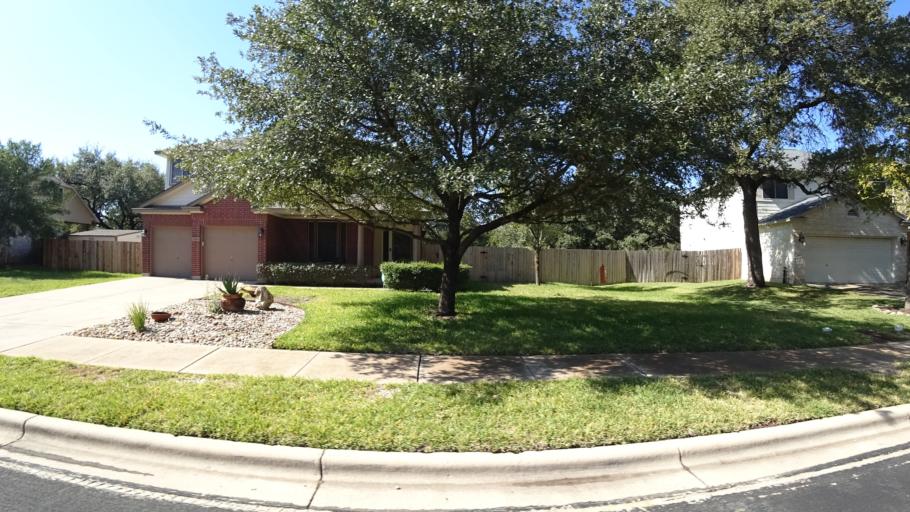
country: US
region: Texas
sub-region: Travis County
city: Shady Hollow
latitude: 30.1975
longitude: -97.8649
